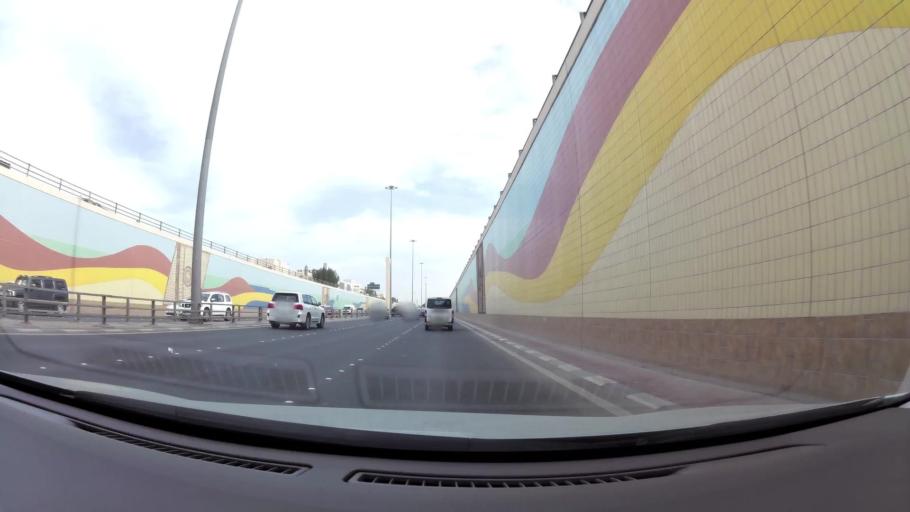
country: QA
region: Baladiyat ad Dawhah
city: Doha
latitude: 25.2635
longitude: 51.4973
